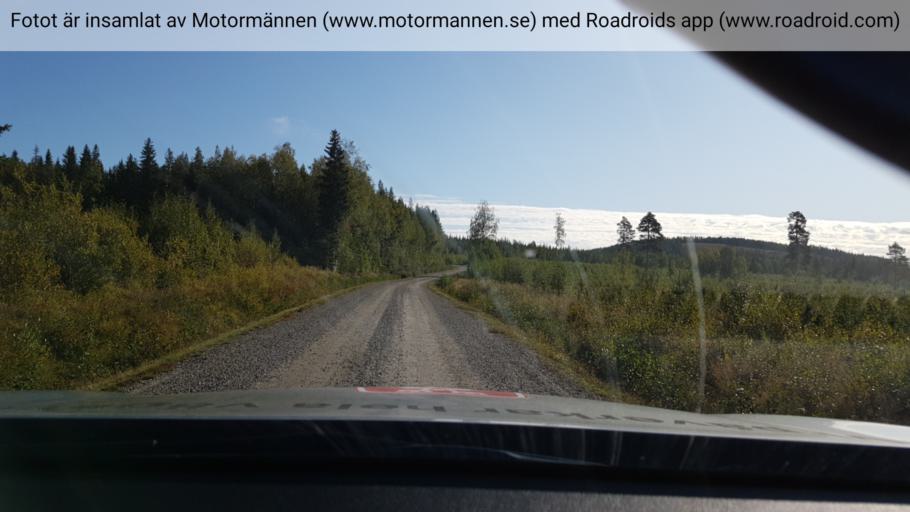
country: SE
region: Vaesterbotten
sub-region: Norsjo Kommun
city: Norsjoe
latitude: 64.6985
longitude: 19.4961
